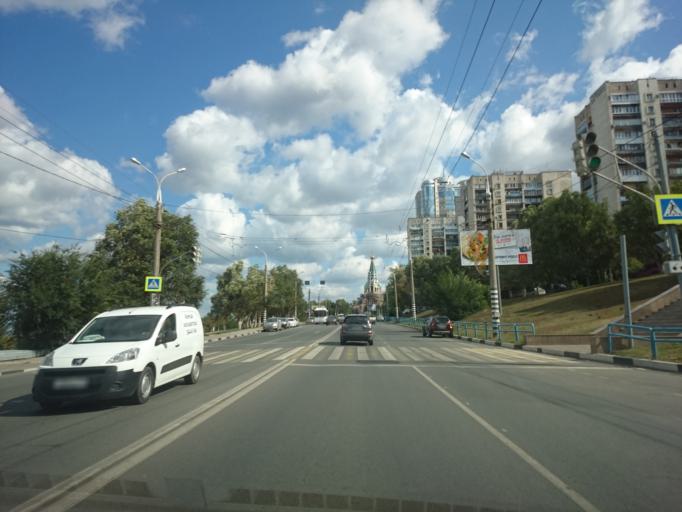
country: RU
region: Samara
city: Samara
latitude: 53.2136
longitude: 50.1290
